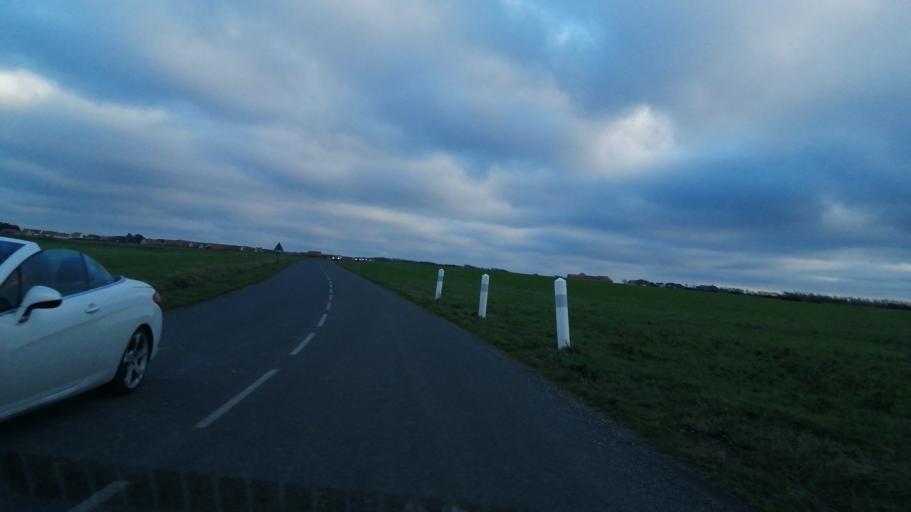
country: FR
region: Nord-Pas-de-Calais
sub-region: Departement du Pas-de-Calais
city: Ambleteuse
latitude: 50.8516
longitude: 1.5954
